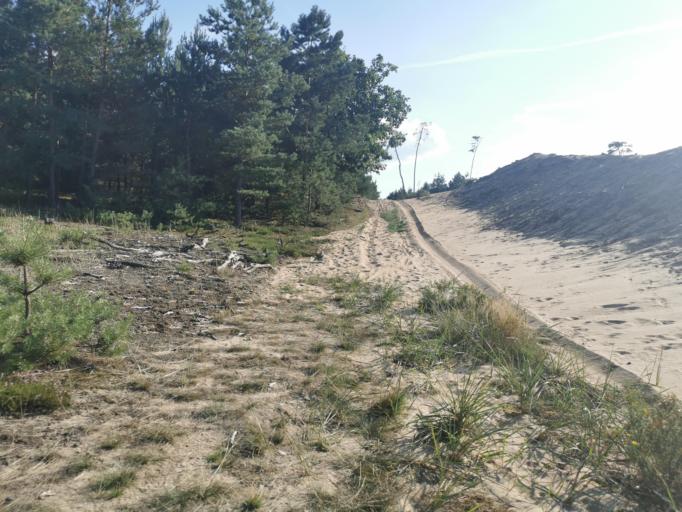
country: SK
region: Trnavsky
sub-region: Okres Senica
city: Senica
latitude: 48.6413
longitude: 17.2956
